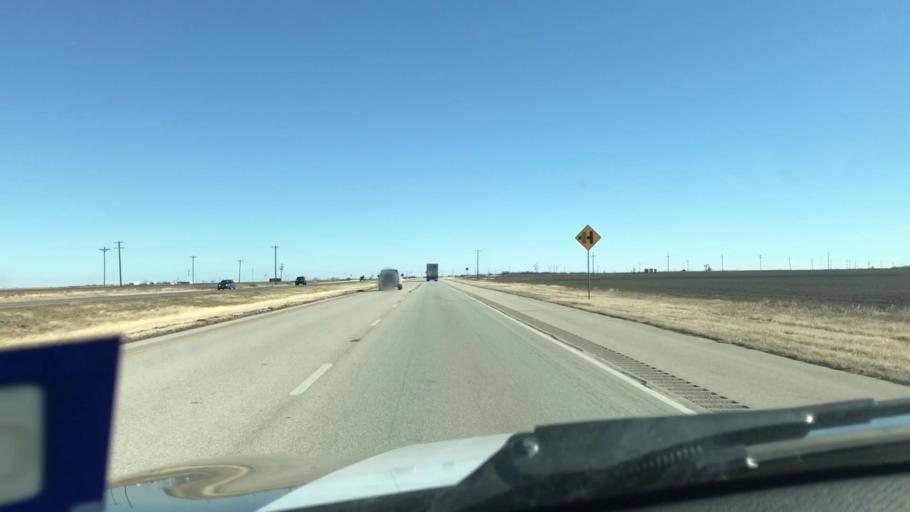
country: US
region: Texas
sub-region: Scurry County
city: Snyder
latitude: 32.6609
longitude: -100.7879
